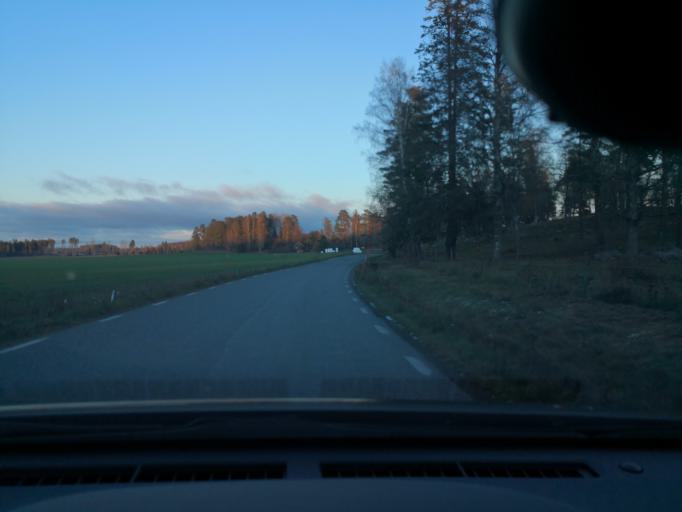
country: SE
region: Vaestmanland
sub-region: Vasteras
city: Tillberga
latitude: 59.7697
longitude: 16.5952
